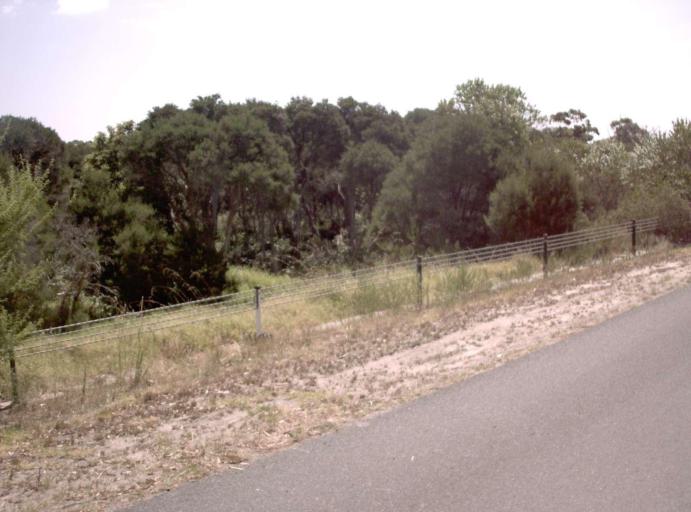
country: AU
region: Victoria
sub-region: Kingston
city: Dingley Village
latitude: -37.9685
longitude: 145.1354
